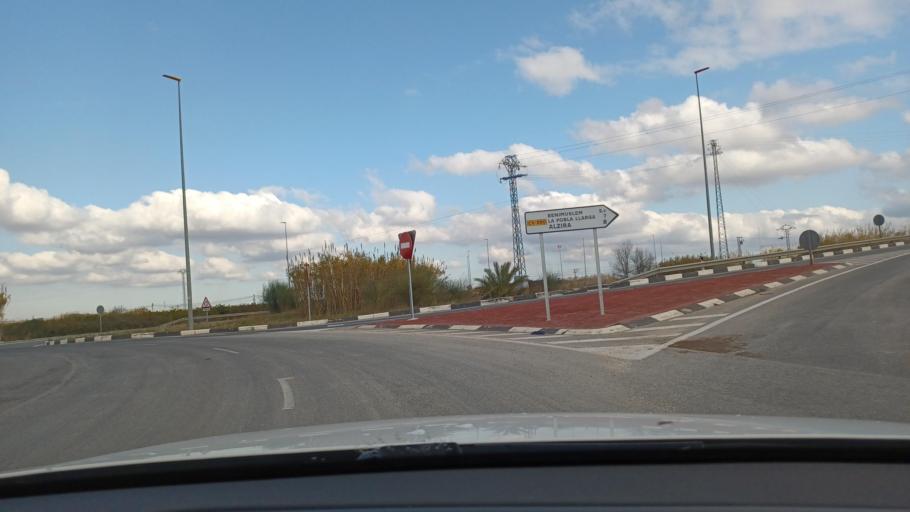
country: ES
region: Valencia
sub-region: Provincia de Valencia
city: Masalaves
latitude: 39.1321
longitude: -0.5219
